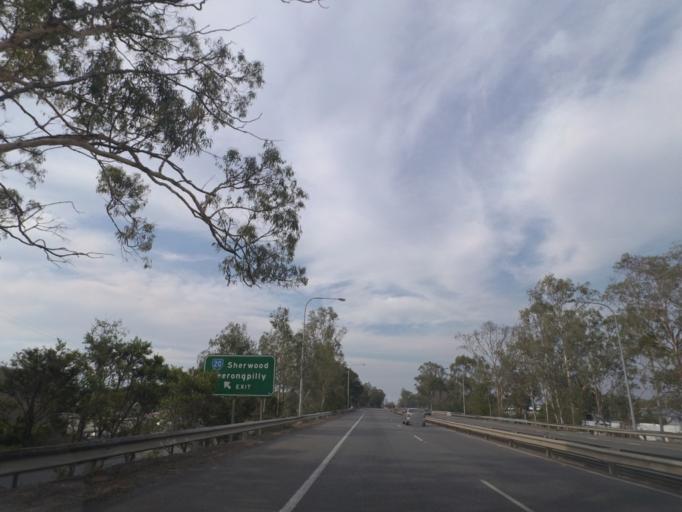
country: AU
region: Queensland
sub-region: Brisbane
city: Rocklea
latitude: -27.5473
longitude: 153.0099
